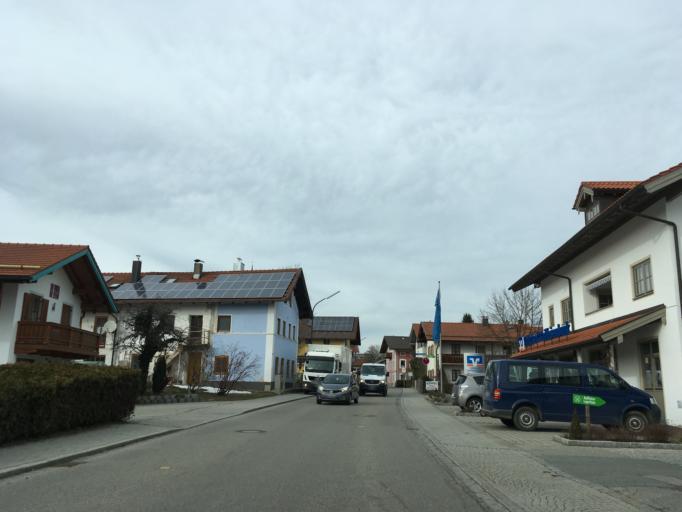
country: DE
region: Bavaria
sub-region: Upper Bavaria
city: Eggstatt
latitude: 47.9241
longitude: 12.3809
